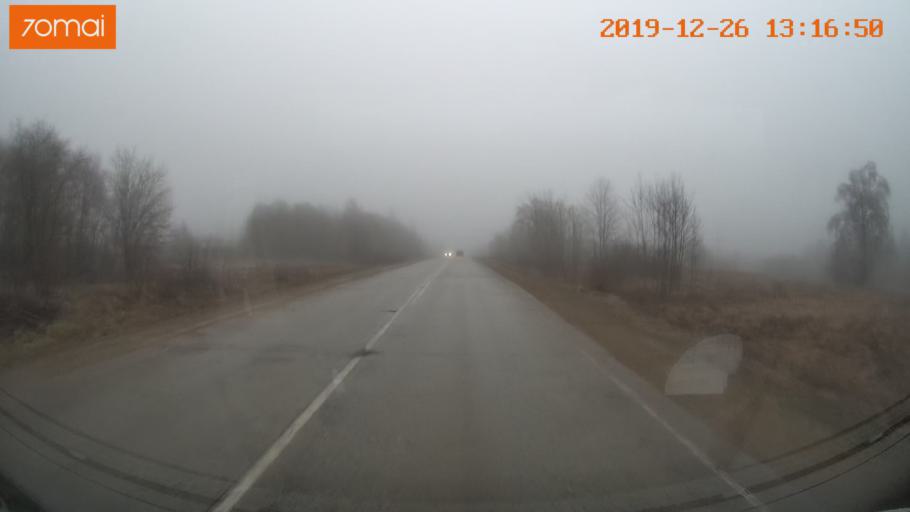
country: RU
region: Vologda
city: Cherepovets
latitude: 58.9768
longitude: 38.1096
